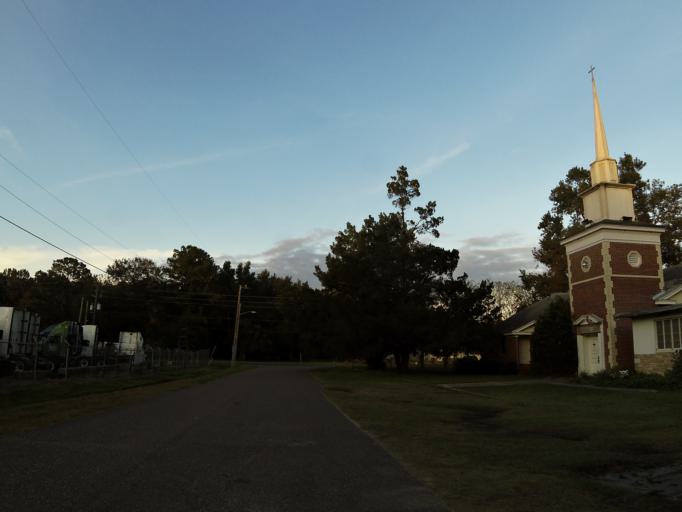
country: US
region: Florida
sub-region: Duval County
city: Jacksonville
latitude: 30.3630
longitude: -81.7363
